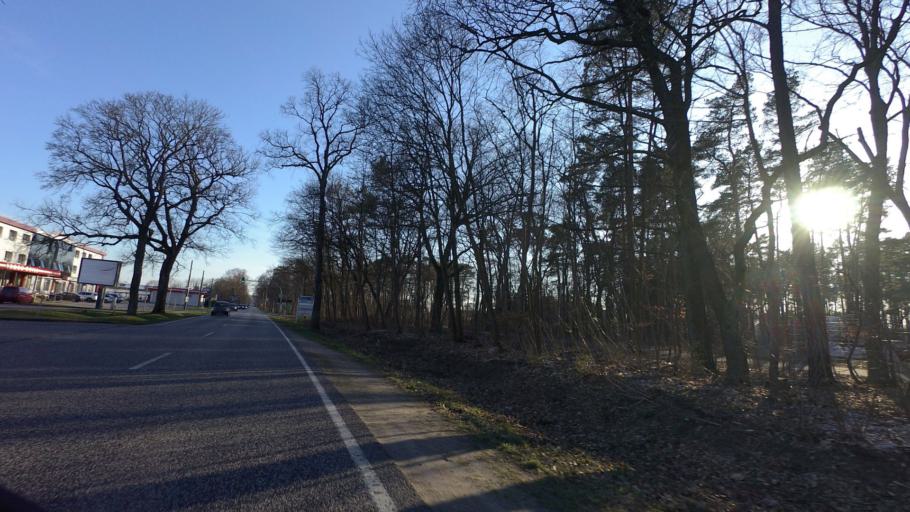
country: DE
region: Brandenburg
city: Eberswalde
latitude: 52.8525
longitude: 13.8260
